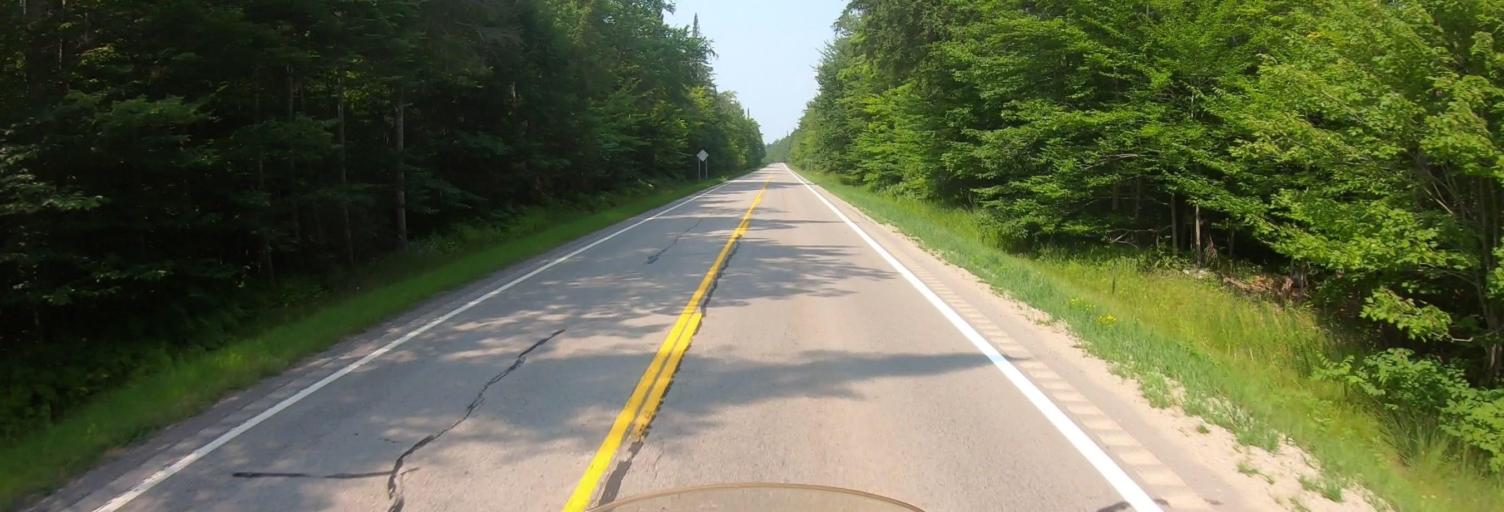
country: US
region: Michigan
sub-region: Luce County
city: Newberry
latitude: 46.5786
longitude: -85.2615
